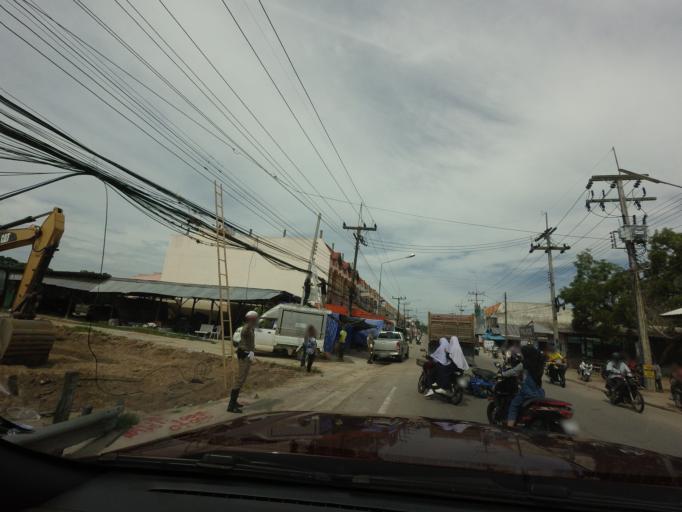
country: TH
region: Narathiwat
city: Tak Bai
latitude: 6.2578
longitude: 102.0517
